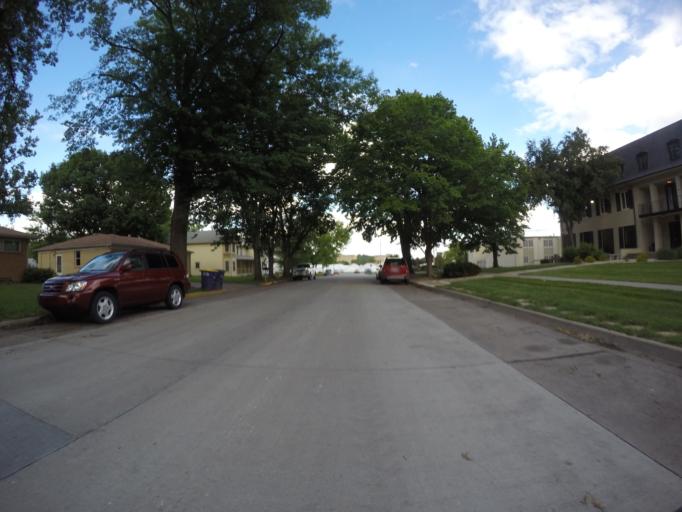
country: US
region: Kansas
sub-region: Riley County
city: Manhattan
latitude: 39.1944
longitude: -96.5869
